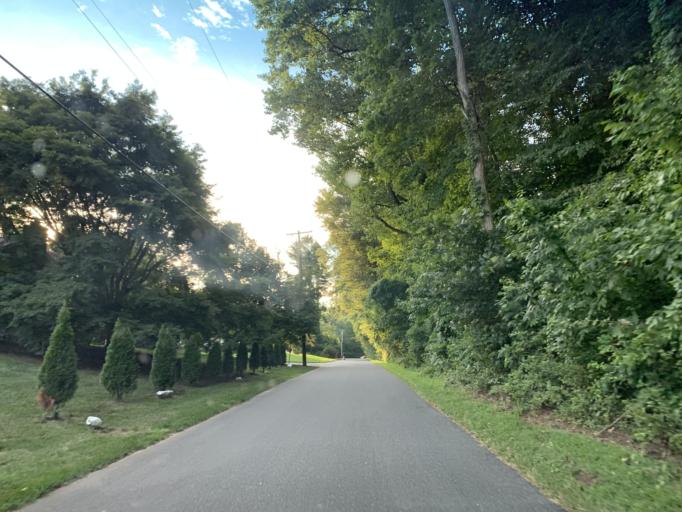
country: US
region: Maryland
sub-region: Harford County
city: Aberdeen
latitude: 39.5208
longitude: -76.1568
